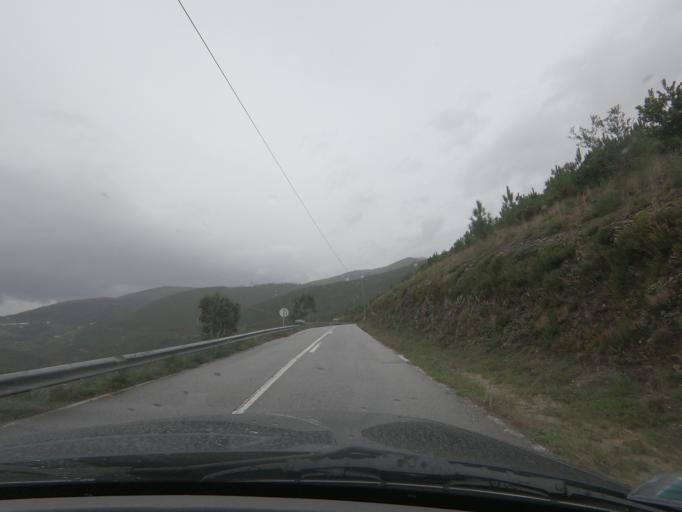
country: PT
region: Vila Real
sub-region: Mondim de Basto
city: Mondim de Basto
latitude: 41.3523
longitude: -7.9180
